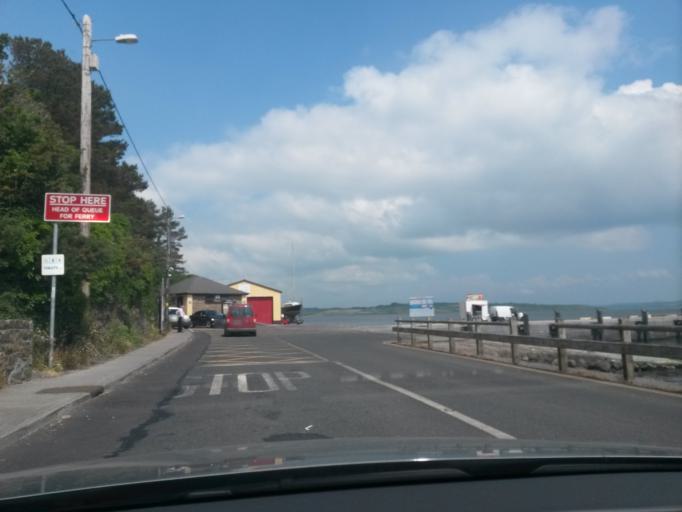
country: IE
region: Munster
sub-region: An Clar
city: Kilrush
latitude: 52.5872
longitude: -9.3604
